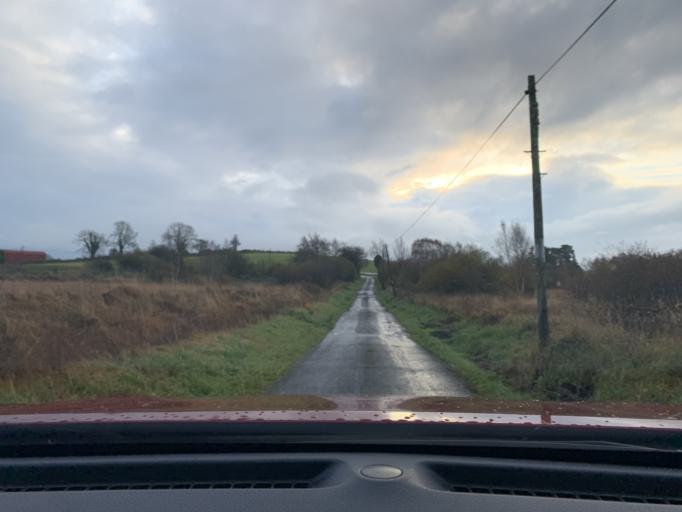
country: IE
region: Connaught
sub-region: Sligo
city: Ballymote
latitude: 54.0295
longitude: -8.5248
